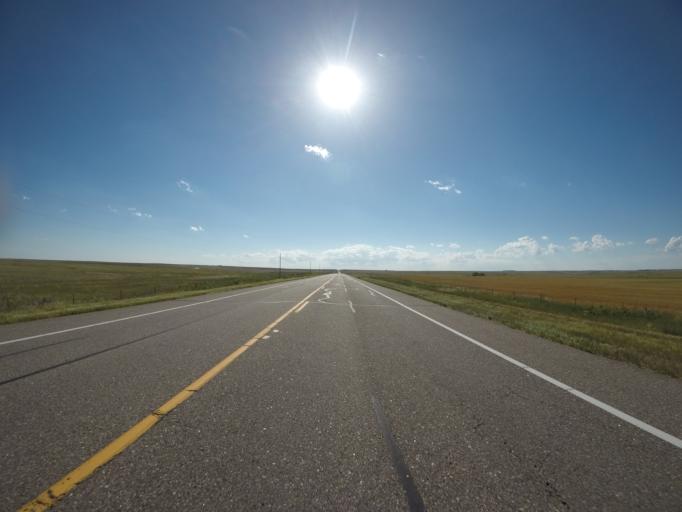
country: US
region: Colorado
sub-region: Logan County
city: Sterling
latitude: 40.6108
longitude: -103.5352
